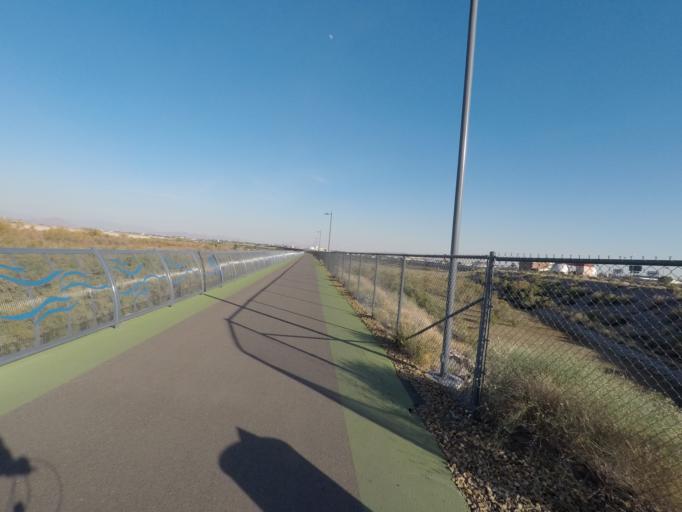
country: US
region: Arizona
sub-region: Maricopa County
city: Tempe
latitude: 33.4365
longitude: -111.8862
